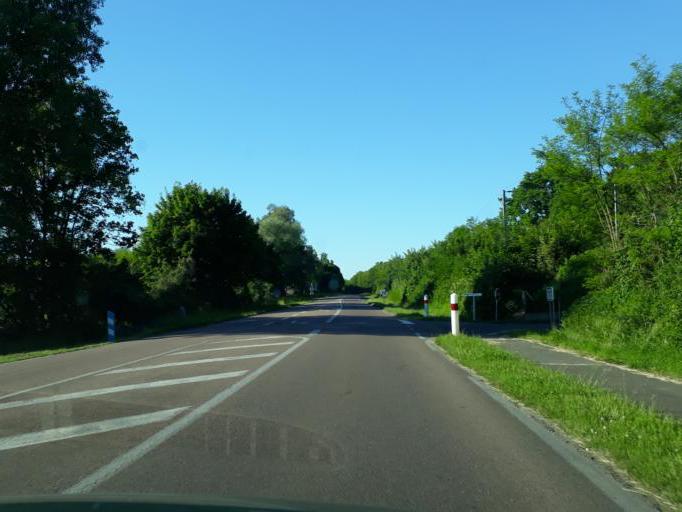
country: FR
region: Bourgogne
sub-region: Departement de la Nievre
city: Cosne-Cours-sur-Loire
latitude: 47.4269
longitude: 2.9320
